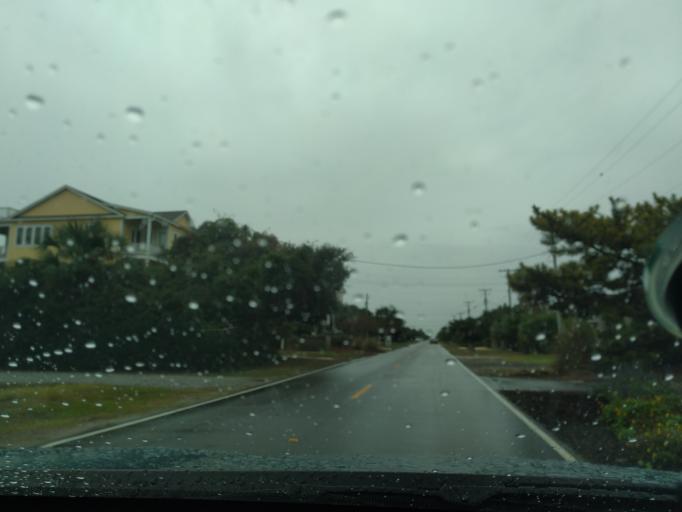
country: US
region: South Carolina
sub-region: Charleston County
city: Folly Beach
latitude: 32.6789
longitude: -79.8954
